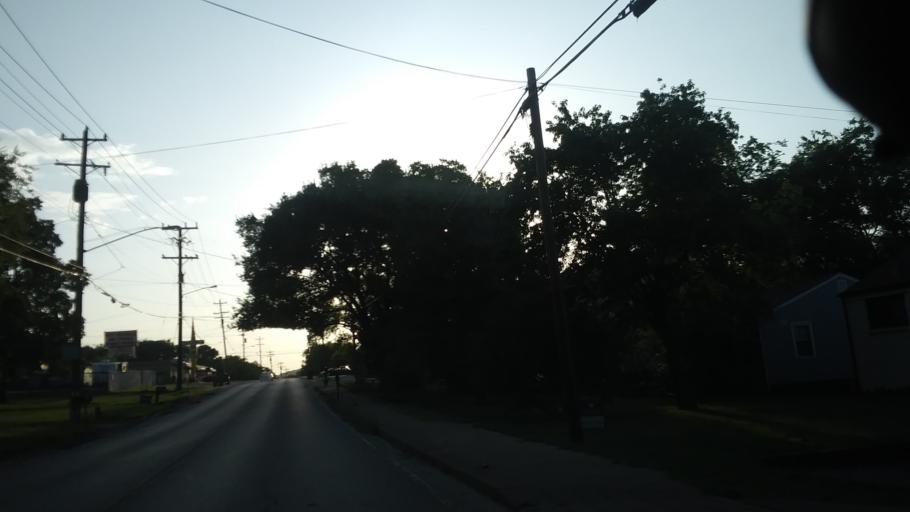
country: US
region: Tennessee
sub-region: Davidson County
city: Belle Meade
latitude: 36.1575
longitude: -86.8727
